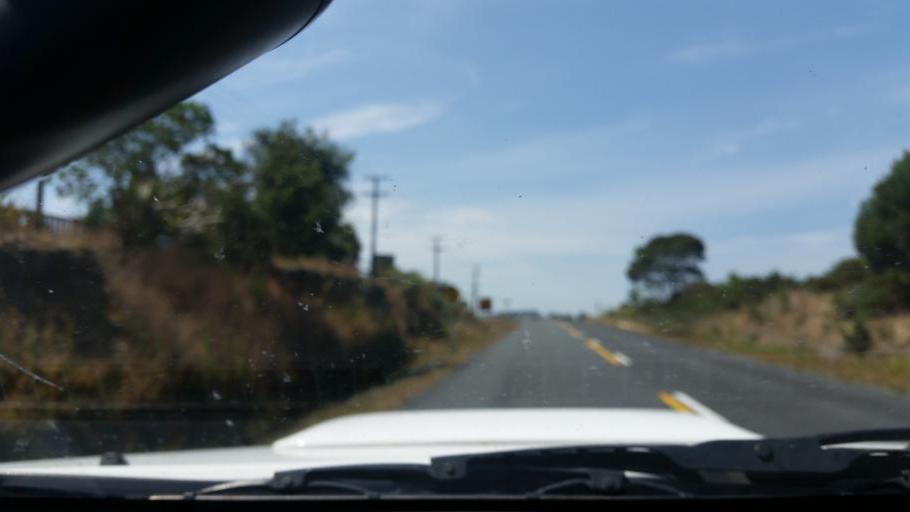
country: NZ
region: Northland
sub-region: Kaipara District
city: Dargaville
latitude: -36.0336
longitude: 173.9211
